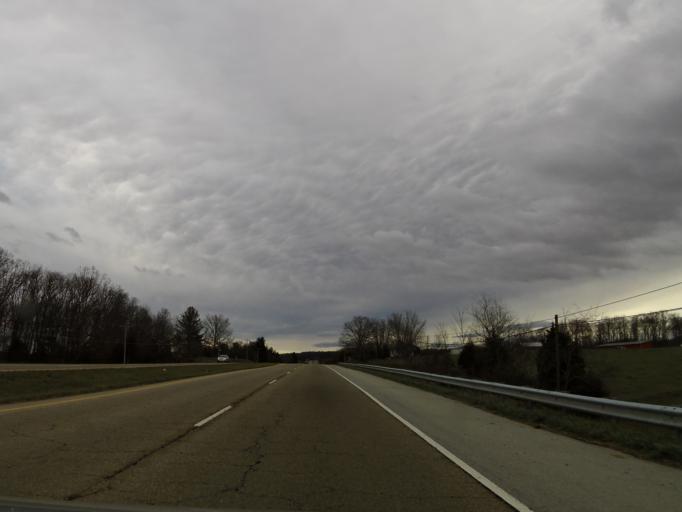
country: US
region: Tennessee
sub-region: Washington County
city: Jonesborough
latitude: 36.2565
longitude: -82.5804
